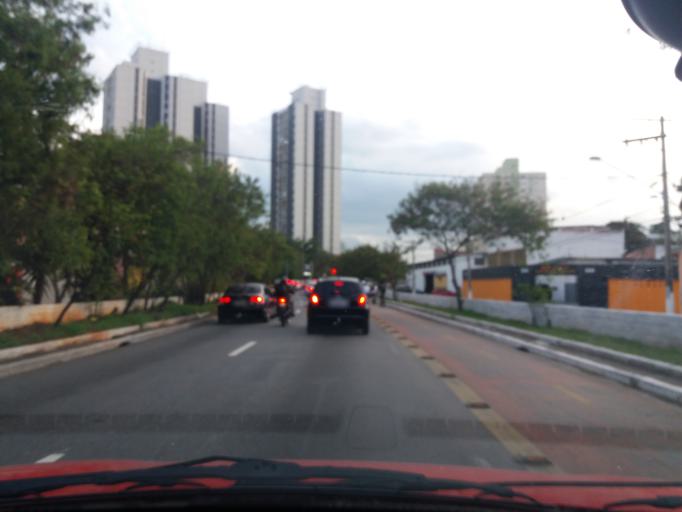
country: BR
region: Sao Paulo
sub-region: Taboao Da Serra
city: Taboao da Serra
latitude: -23.6034
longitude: -46.7488
